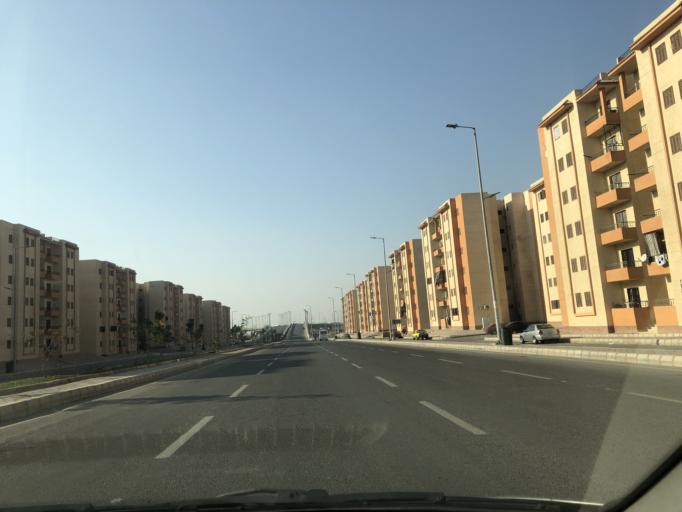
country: EG
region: Al Jizah
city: Madinat Sittah Uktubar
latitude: 29.8891
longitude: 30.8981
